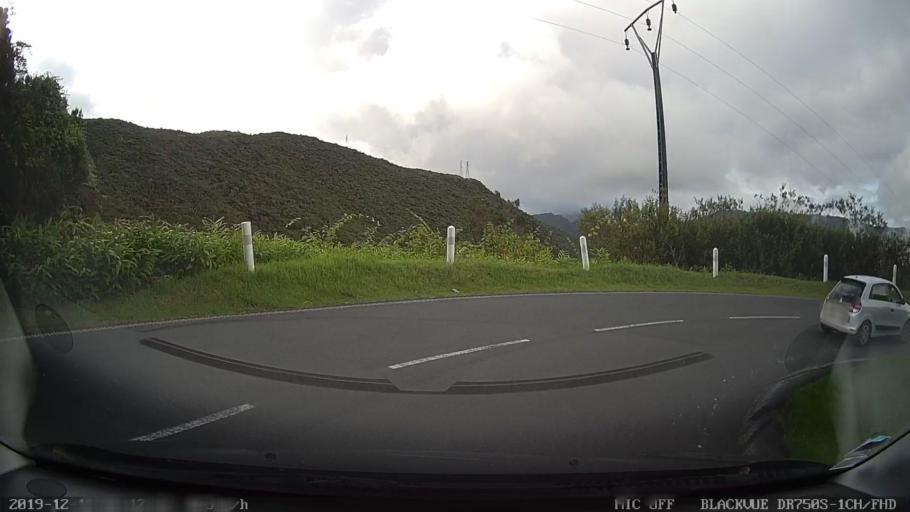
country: RE
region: Reunion
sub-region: Reunion
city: Cilaos
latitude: -21.1613
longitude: 55.5923
